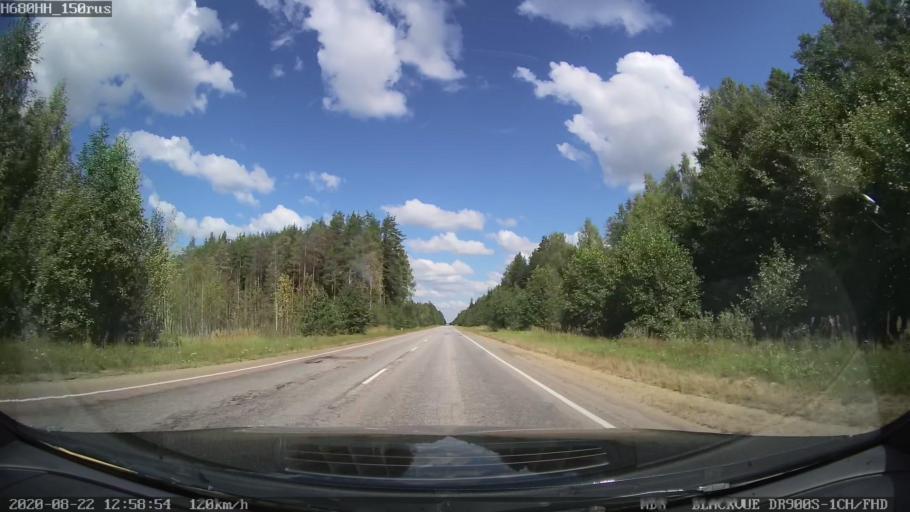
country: RU
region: Tverskaya
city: Bezhetsk
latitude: 57.5975
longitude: 36.3522
